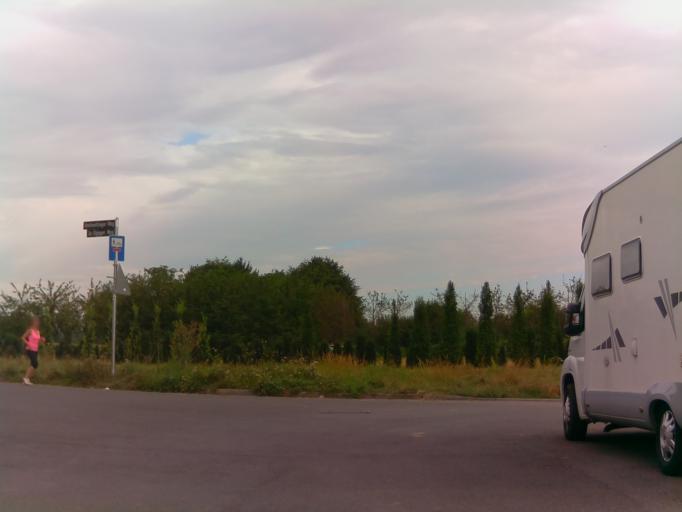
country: DE
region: Baden-Wuerttemberg
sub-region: Regierungsbezirk Stuttgart
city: Leinfelden-Echterdingen
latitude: 48.7336
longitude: 9.1405
